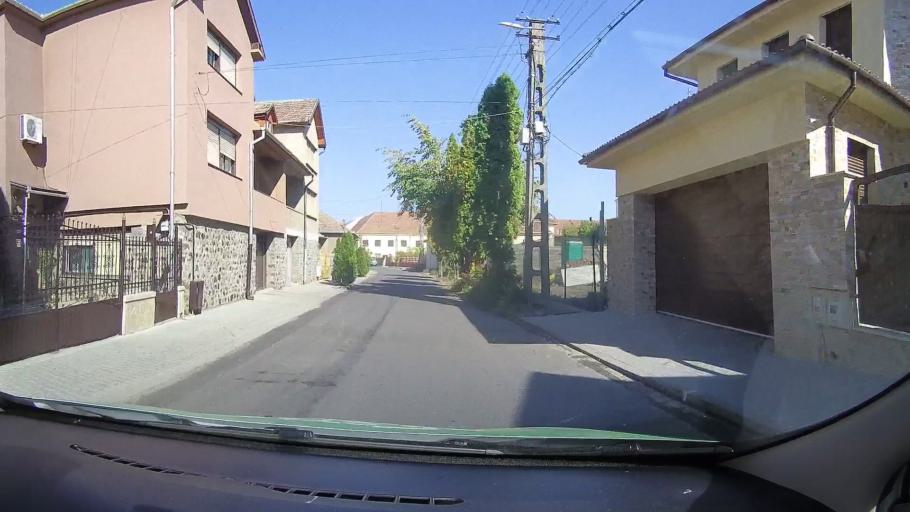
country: RO
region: Satu Mare
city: Carei
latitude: 47.6864
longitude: 22.4662
